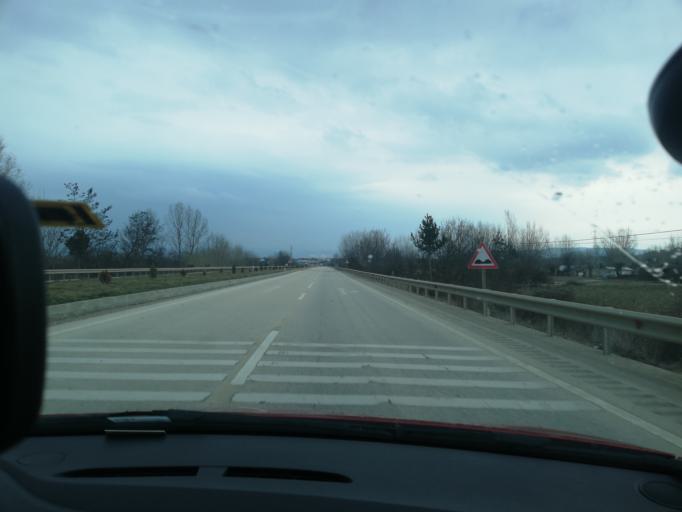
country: TR
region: Kastamonu
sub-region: Cide
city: Kastamonu
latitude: 41.4875
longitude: 33.7626
